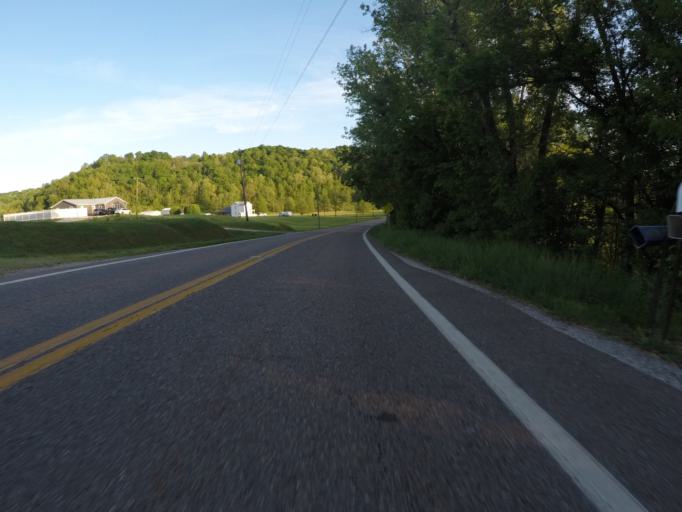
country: US
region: West Virginia
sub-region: Cabell County
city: Huntington
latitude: 38.5135
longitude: -82.4739
